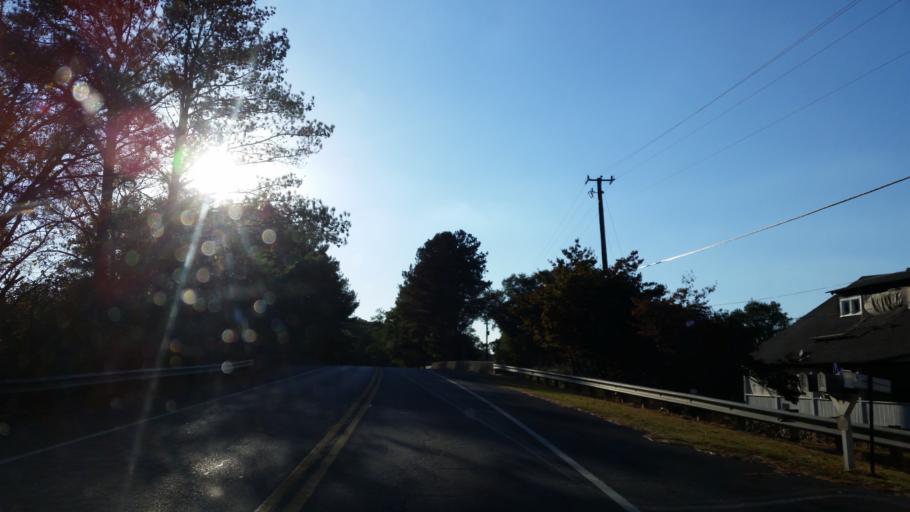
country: US
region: Georgia
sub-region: Bartow County
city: Euharlee
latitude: 34.2389
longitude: -84.9503
